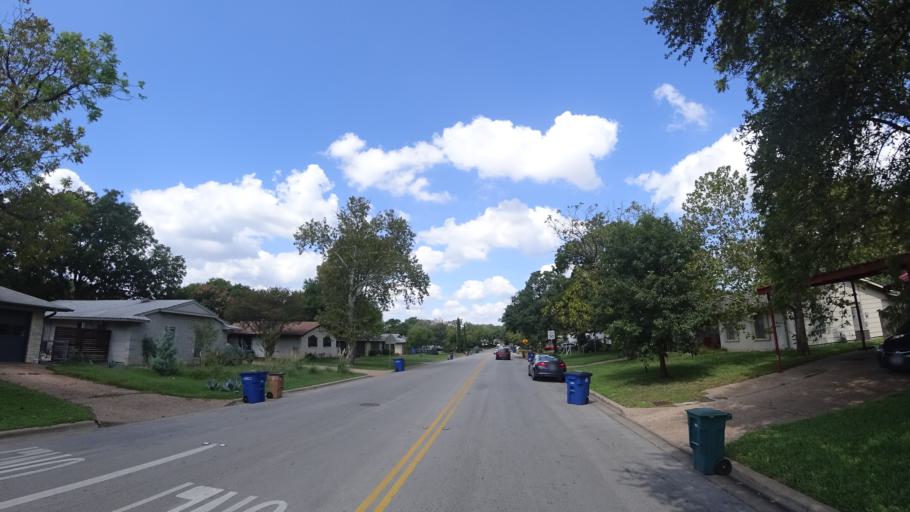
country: US
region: Texas
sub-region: Travis County
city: Wells Branch
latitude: 30.3622
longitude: -97.7215
